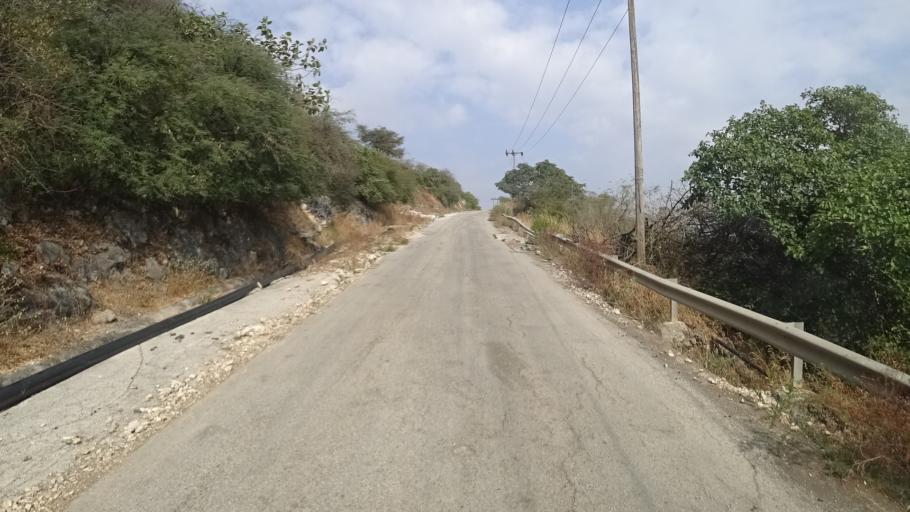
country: YE
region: Al Mahrah
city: Hawf
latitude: 16.7256
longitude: 53.2741
